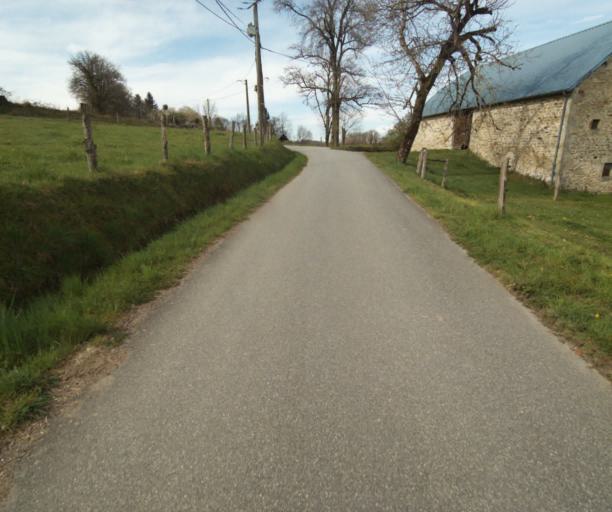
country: FR
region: Limousin
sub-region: Departement de la Correze
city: Correze
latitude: 45.3516
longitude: 1.8598
